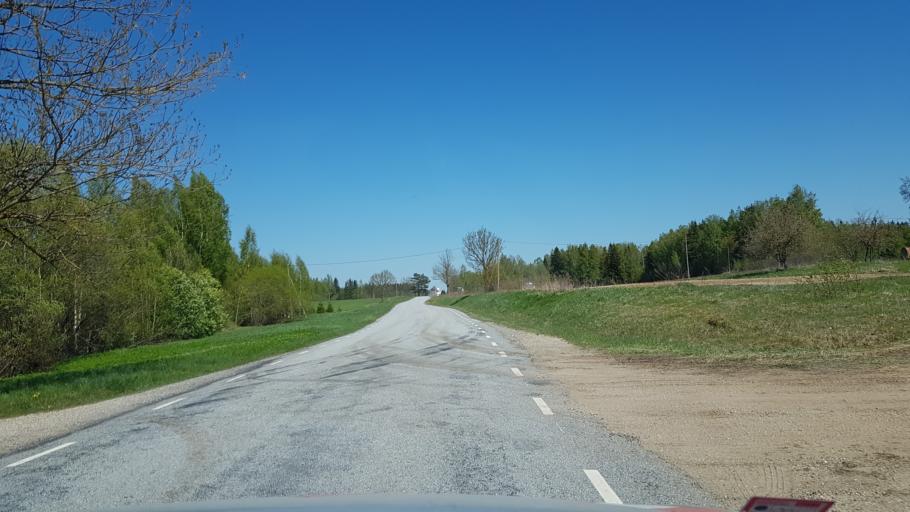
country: EE
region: Vorumaa
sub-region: Voru linn
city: Voru
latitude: 57.9266
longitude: 26.9511
